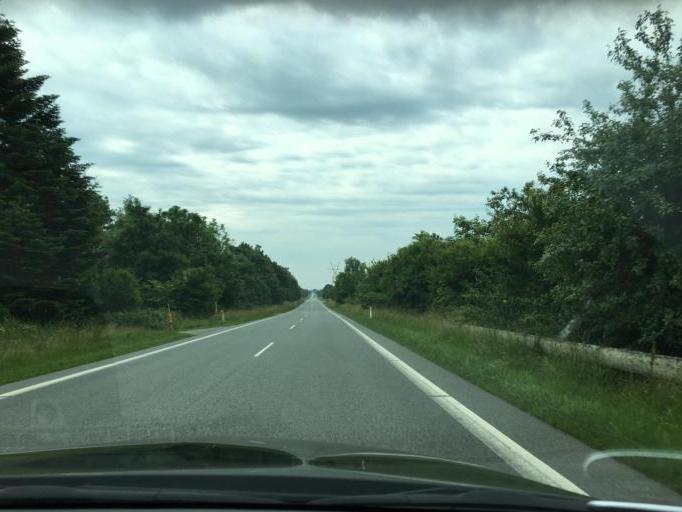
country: DK
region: South Denmark
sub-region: Vejle Kommune
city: Vejle
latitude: 55.6099
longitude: 9.4968
